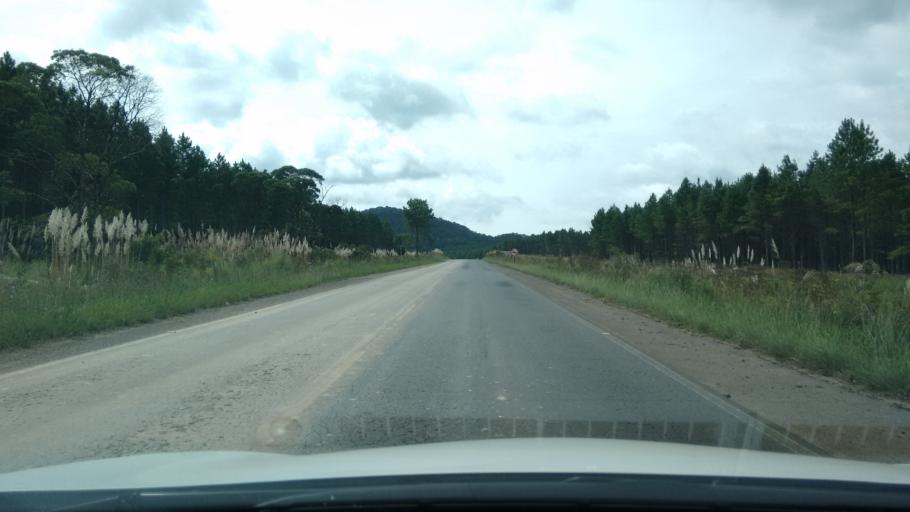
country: BR
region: Santa Catarina
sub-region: Otacilio Costa
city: Otacilio Costa
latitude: -27.2929
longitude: -50.1899
